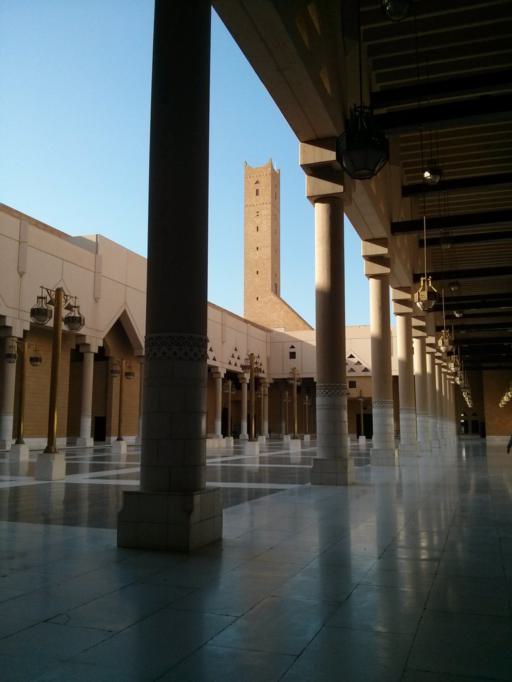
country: SA
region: Ar Riyad
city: Riyadh
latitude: 24.6311
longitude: 46.7128
